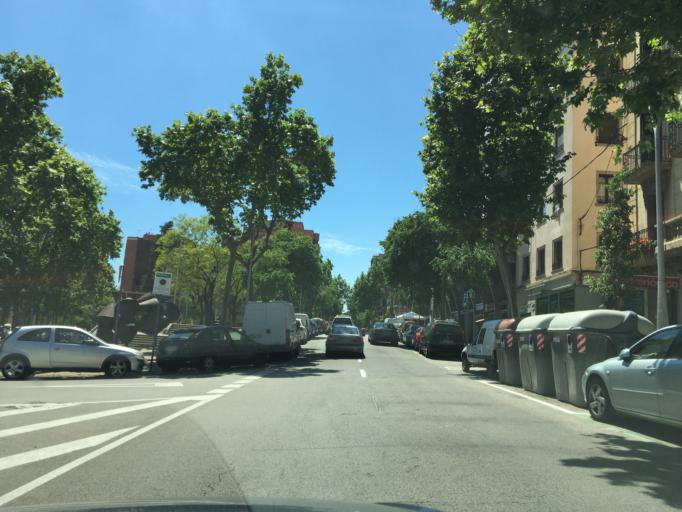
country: ES
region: Catalonia
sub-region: Provincia de Barcelona
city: Horta-Guinardo
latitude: 41.4127
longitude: 2.1809
